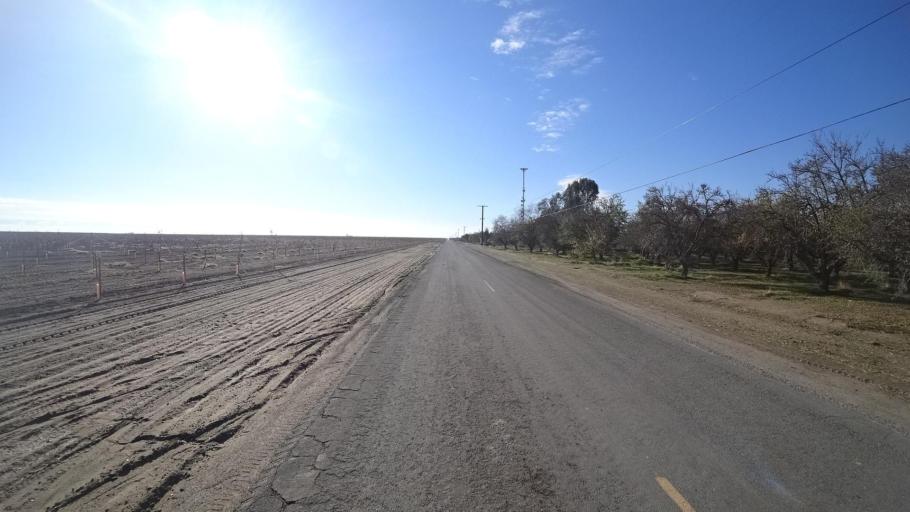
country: US
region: California
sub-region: Kern County
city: Delano
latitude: 35.7569
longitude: -119.3119
